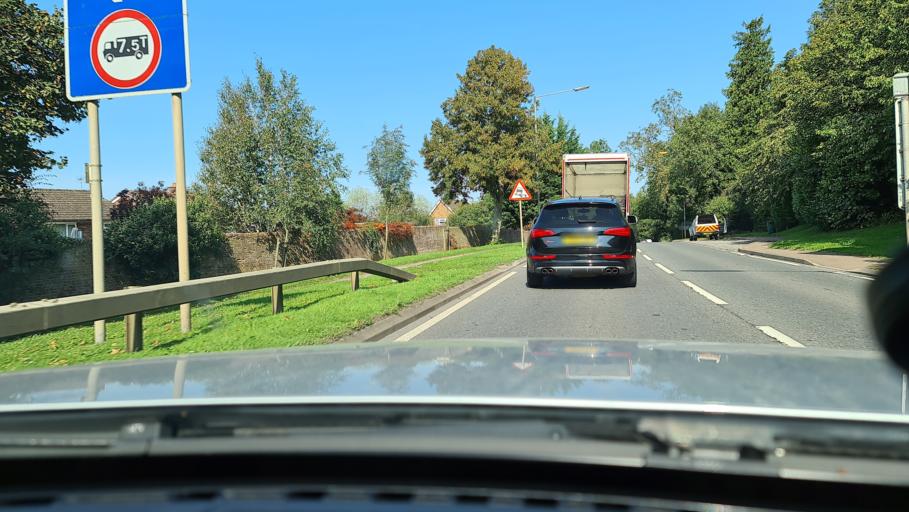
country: GB
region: England
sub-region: Northamptonshire
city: Daventry
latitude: 52.3356
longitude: -1.1735
